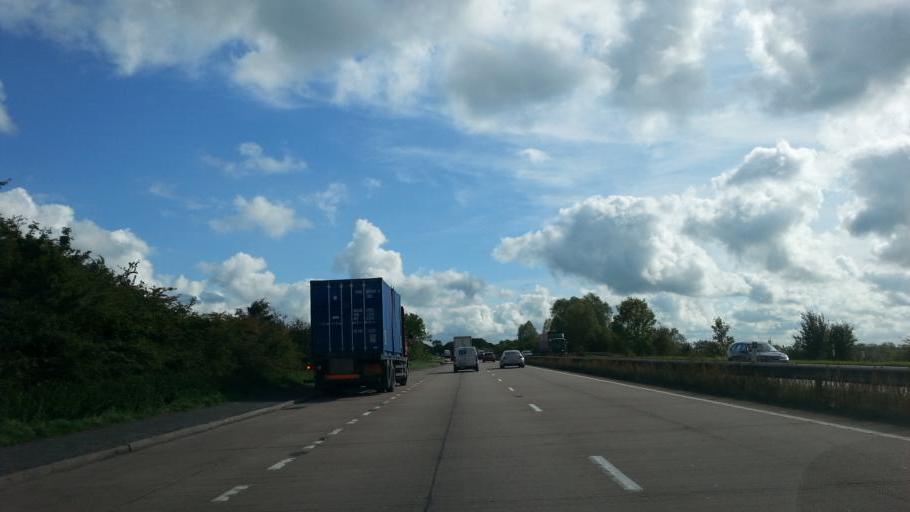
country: GB
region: England
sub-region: Staffordshire
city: Cheadle
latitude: 52.9471
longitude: -2.0109
